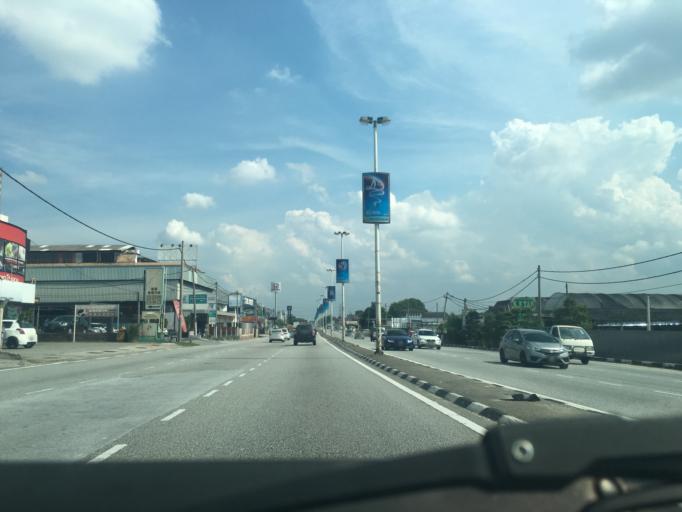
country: MY
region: Perak
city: Ipoh
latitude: 4.6271
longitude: 101.0822
